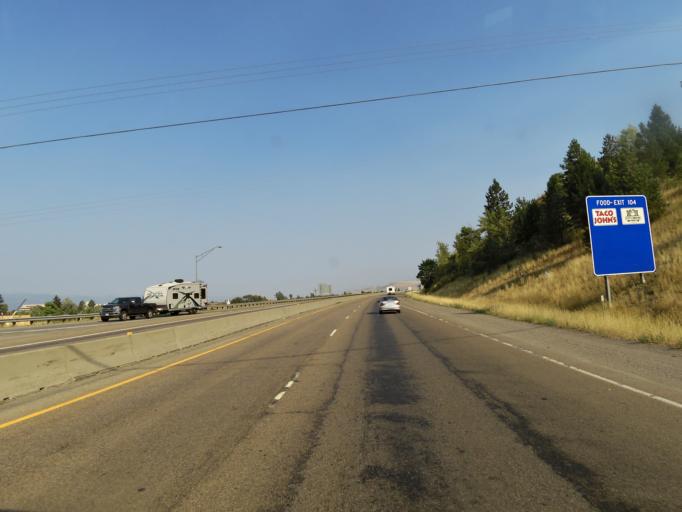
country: US
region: Montana
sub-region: Missoula County
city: Missoula
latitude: 46.8727
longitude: -113.9842
